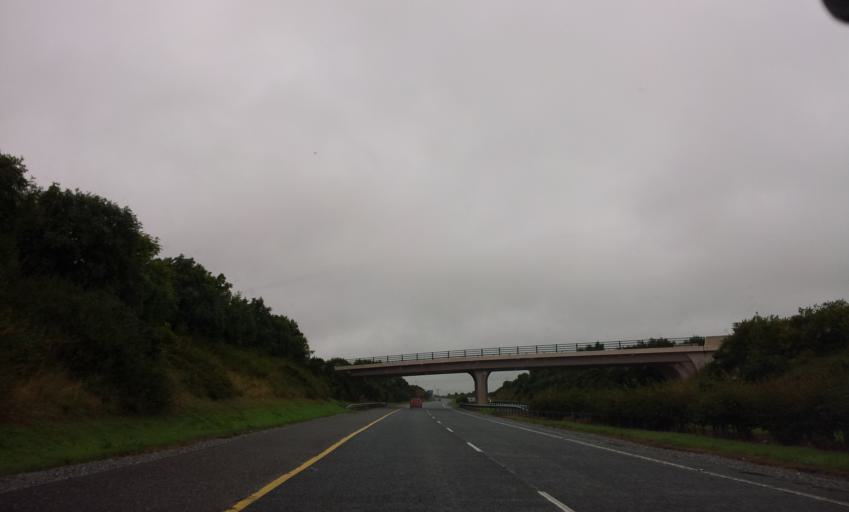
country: IE
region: Munster
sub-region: County Cork
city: Watergrasshill
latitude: 51.9948
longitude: -8.3562
